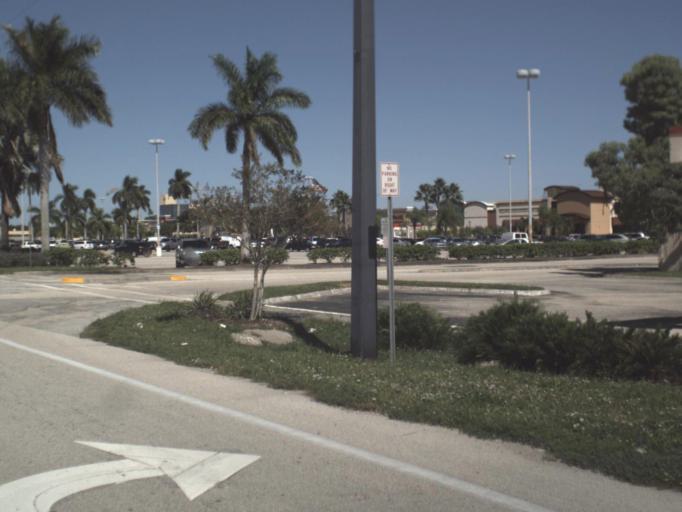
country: US
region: Florida
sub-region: Lee County
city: Pine Manor
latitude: 26.6001
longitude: -81.8716
